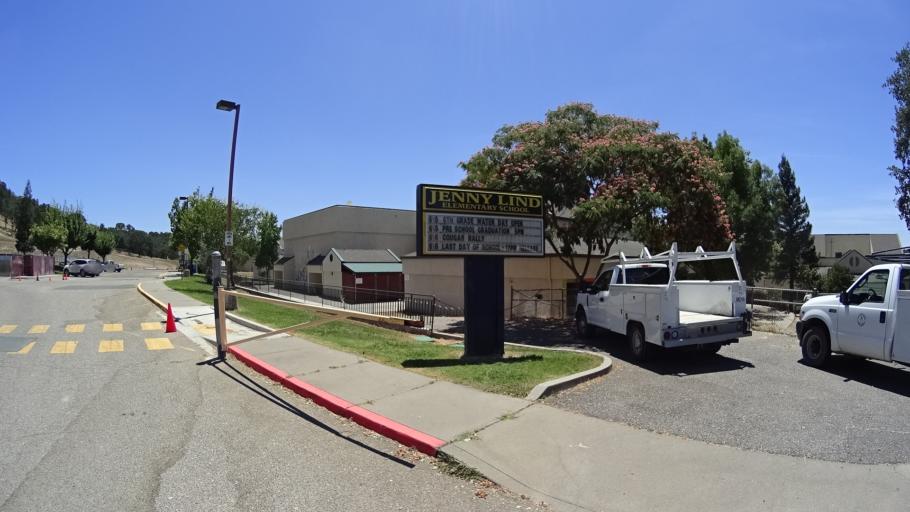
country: US
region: California
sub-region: Calaveras County
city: Rancho Calaveras
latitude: 38.1349
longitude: -120.8660
